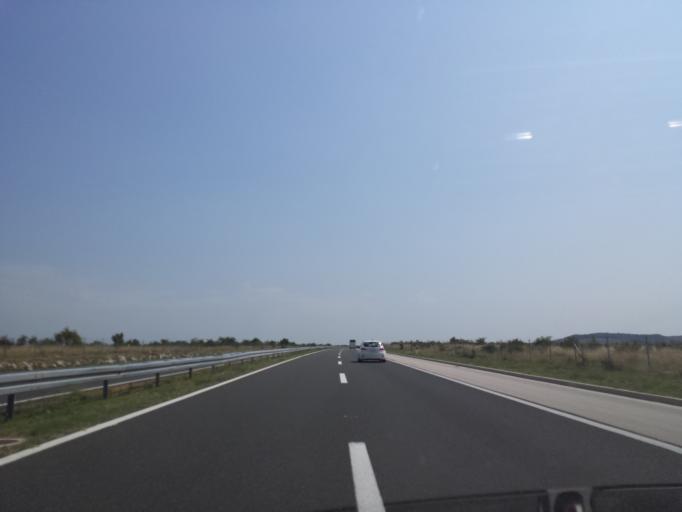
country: HR
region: Zadarska
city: Polaca
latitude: 44.0926
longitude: 15.4867
